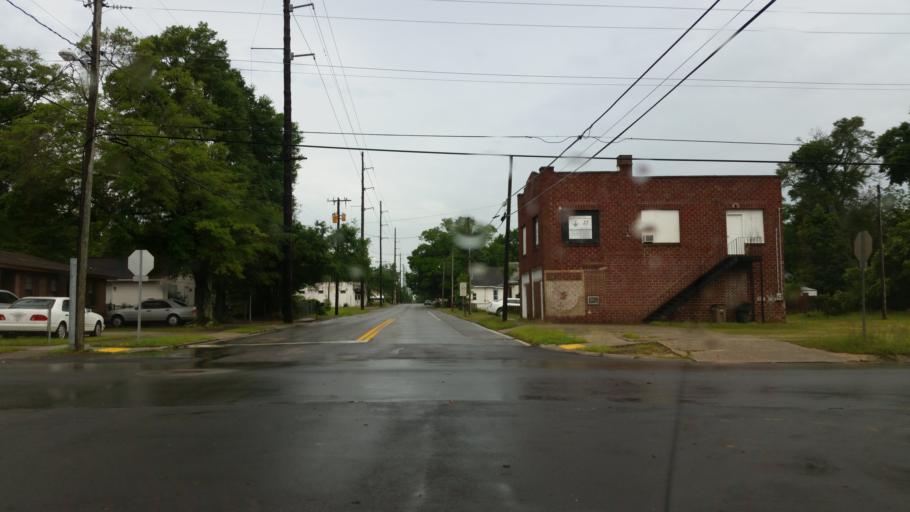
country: US
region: Florida
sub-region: Escambia County
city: Pensacola
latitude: 30.4182
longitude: -87.2300
